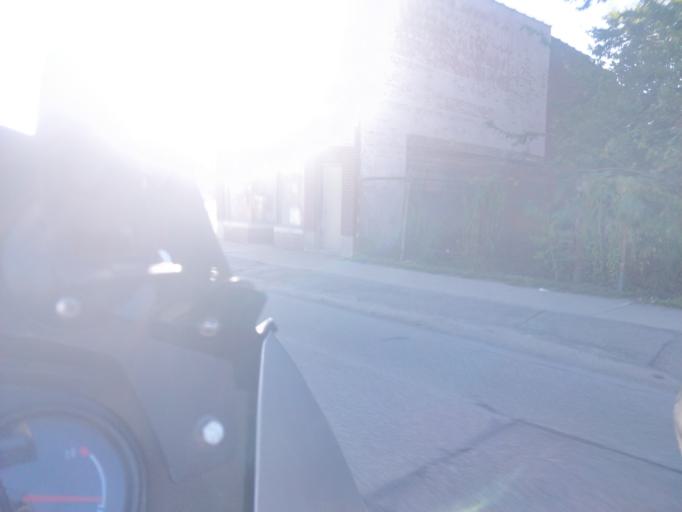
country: US
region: Michigan
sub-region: Wayne County
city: Melvindale
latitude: 42.2783
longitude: -83.1906
